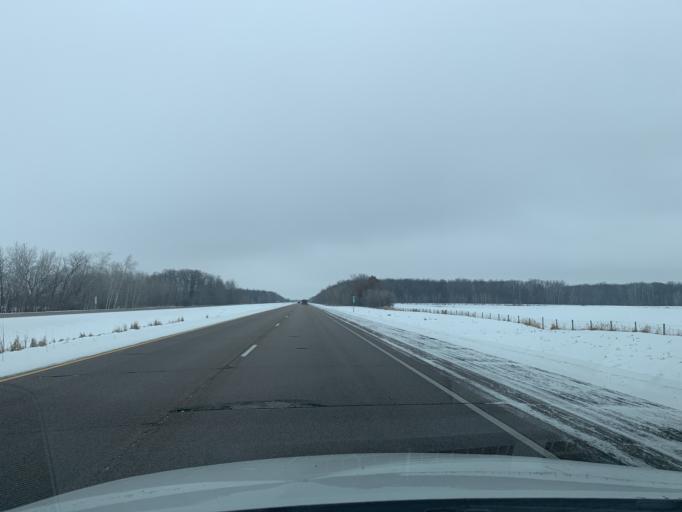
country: US
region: Minnesota
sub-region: Chisago County
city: Rush City
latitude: 45.6549
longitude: -92.9922
